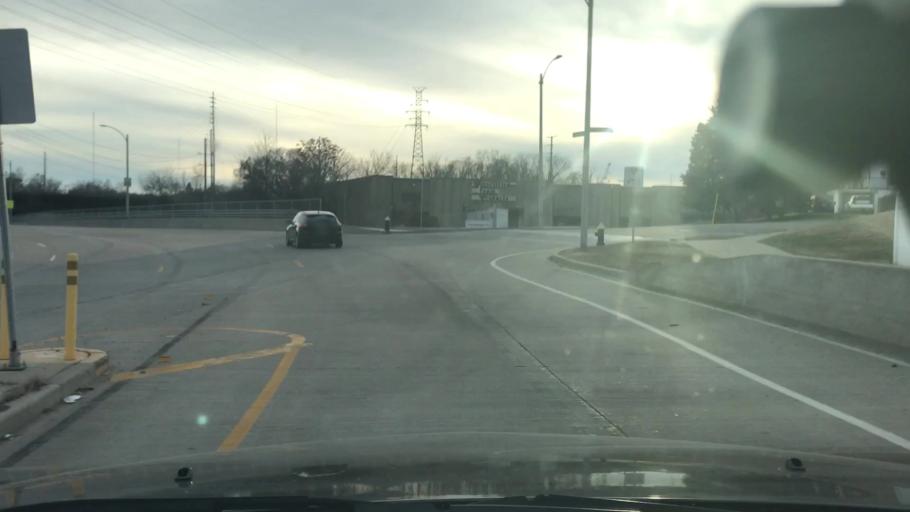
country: US
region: Missouri
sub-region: Saint Louis County
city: Maplewood
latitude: 38.6020
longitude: -90.3153
